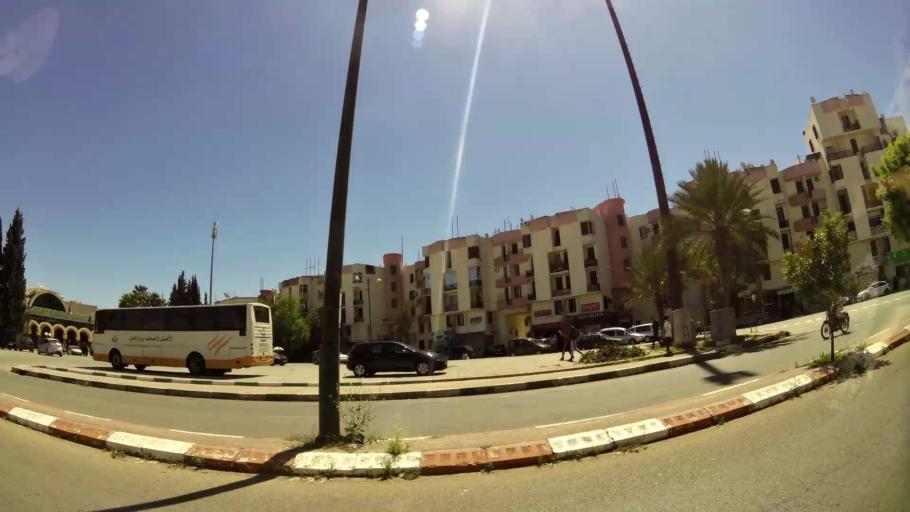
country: MA
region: Meknes-Tafilalet
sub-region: Meknes
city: Meknes
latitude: 33.9029
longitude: -5.5324
